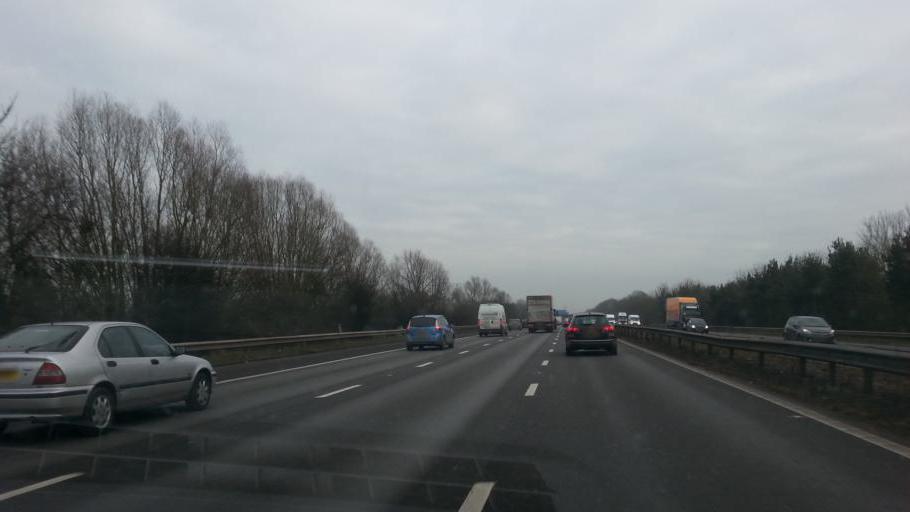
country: GB
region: England
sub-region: Warwickshire
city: Exhall
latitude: 52.4473
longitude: -1.4584
